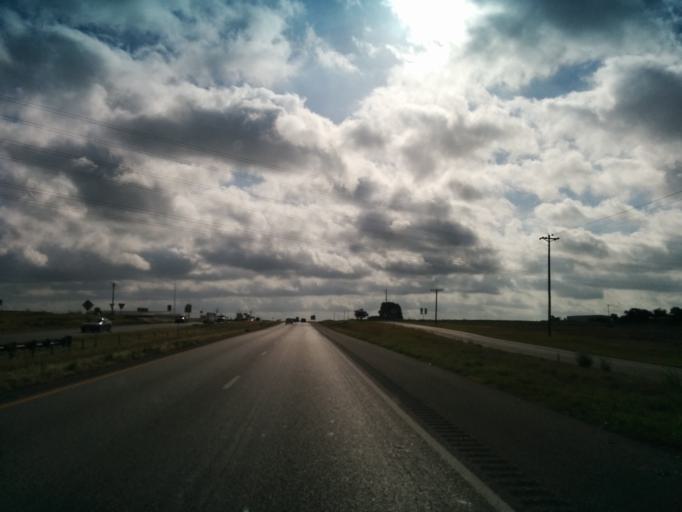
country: US
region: Texas
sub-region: Guadalupe County
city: Marion
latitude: 29.5362
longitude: -98.0851
